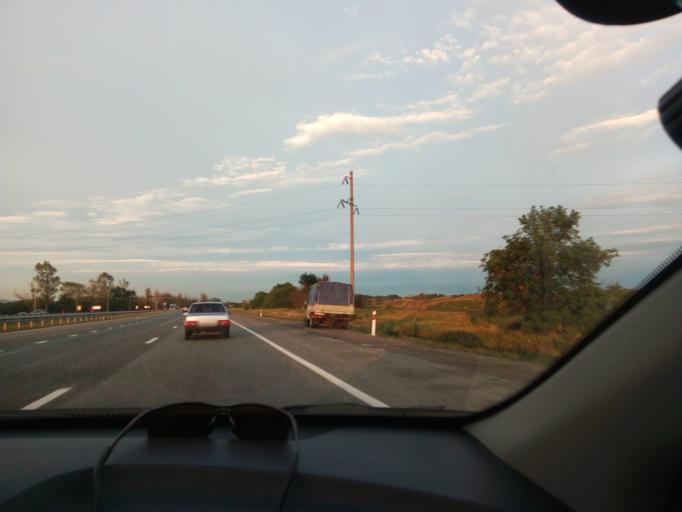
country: RU
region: Stavropol'skiy
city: Barsukovskaya
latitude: 44.7129
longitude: 41.8455
